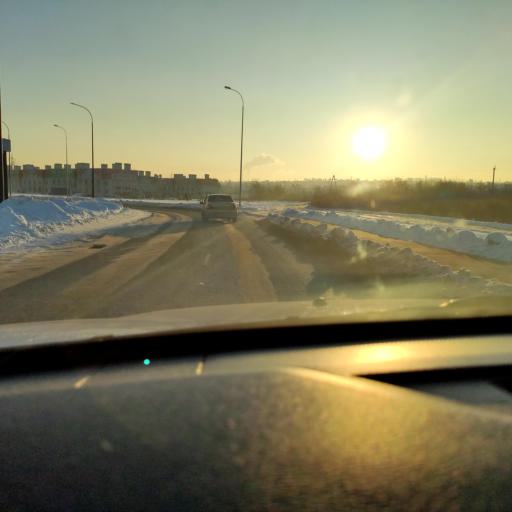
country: RU
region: Samara
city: Petra-Dubrava
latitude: 53.2989
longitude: 50.3167
